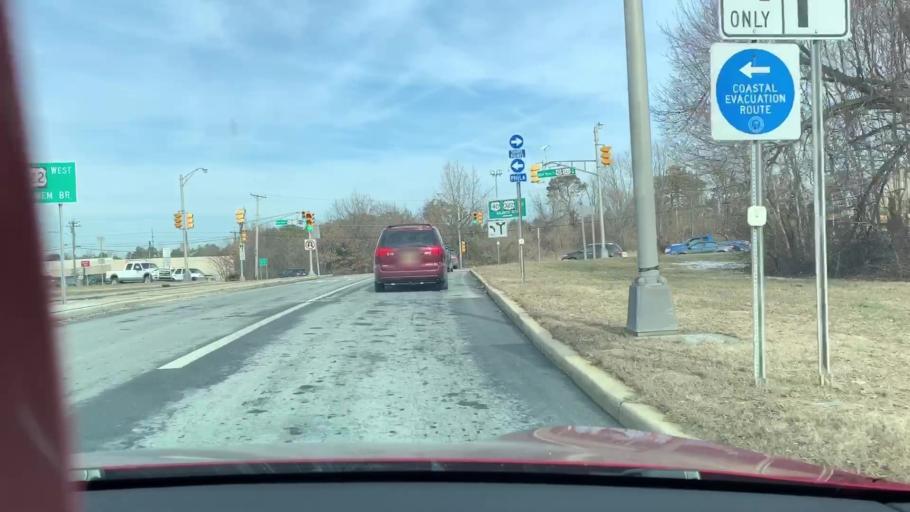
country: US
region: New Jersey
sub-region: Atlantic County
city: Northfield
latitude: 39.4001
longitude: -74.5612
